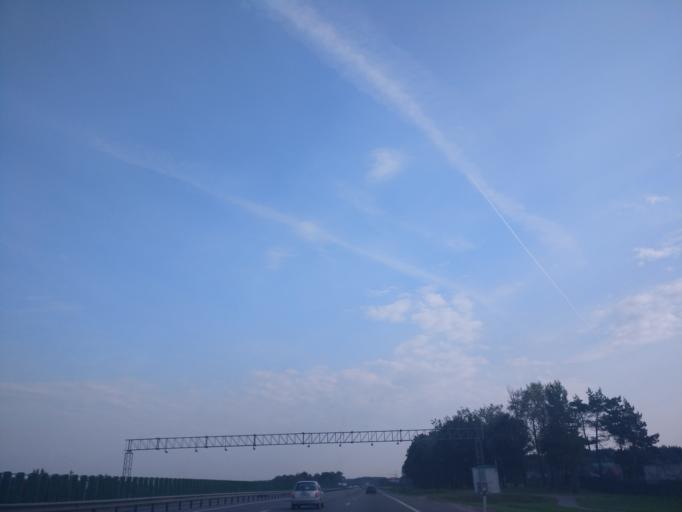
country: BY
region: Minsk
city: Borovlyany
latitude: 53.9696
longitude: 27.6465
